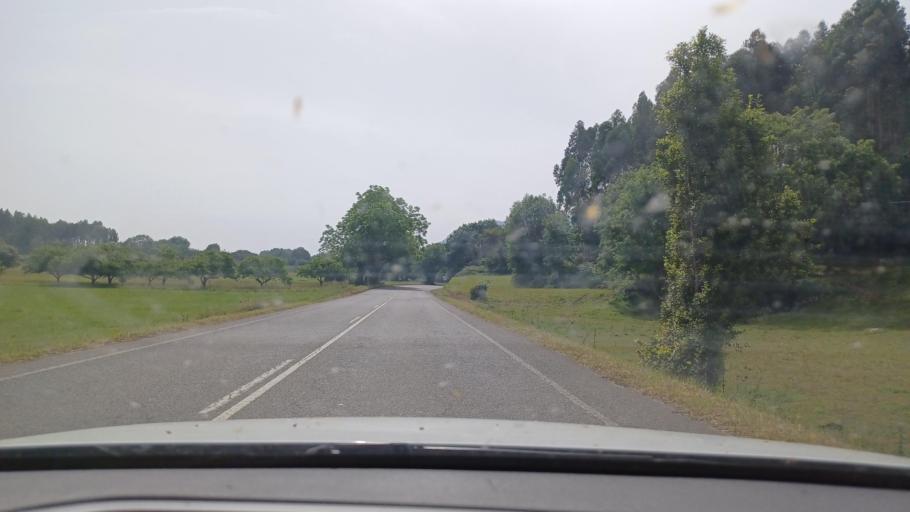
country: ES
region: Asturias
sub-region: Province of Asturias
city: Ribadesella
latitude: 43.4523
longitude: -5.0281
